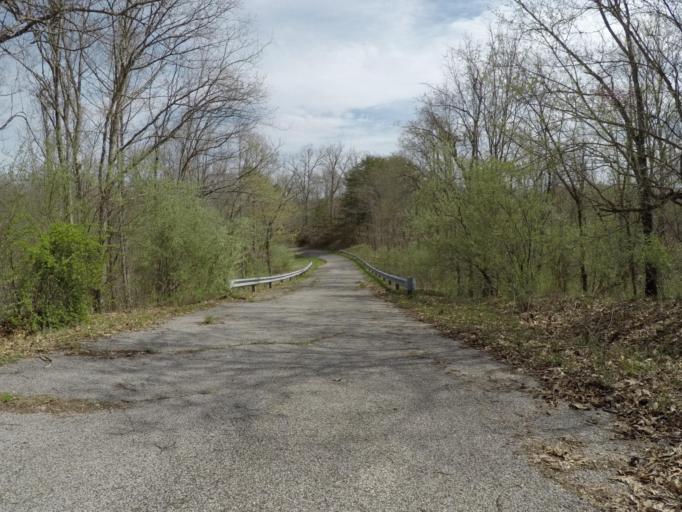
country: US
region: West Virginia
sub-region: Wayne County
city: Lavalette
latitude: 38.3166
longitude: -82.3514
